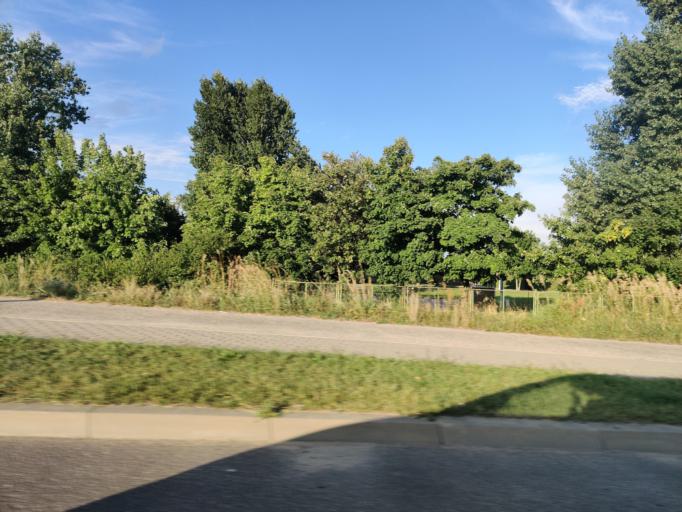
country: PL
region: Greater Poland Voivodeship
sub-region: Konin
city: Konin
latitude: 52.2191
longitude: 18.2528
